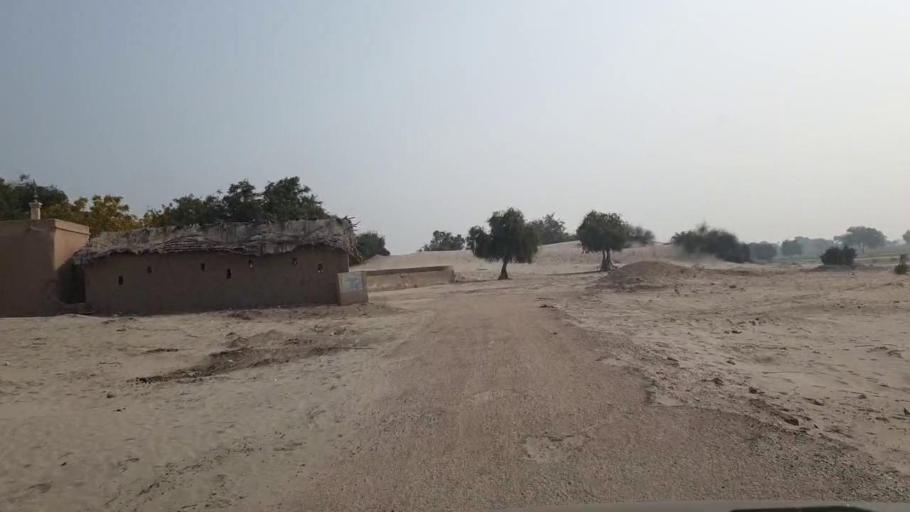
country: PK
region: Sindh
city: Hala
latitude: 25.8248
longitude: 68.4464
